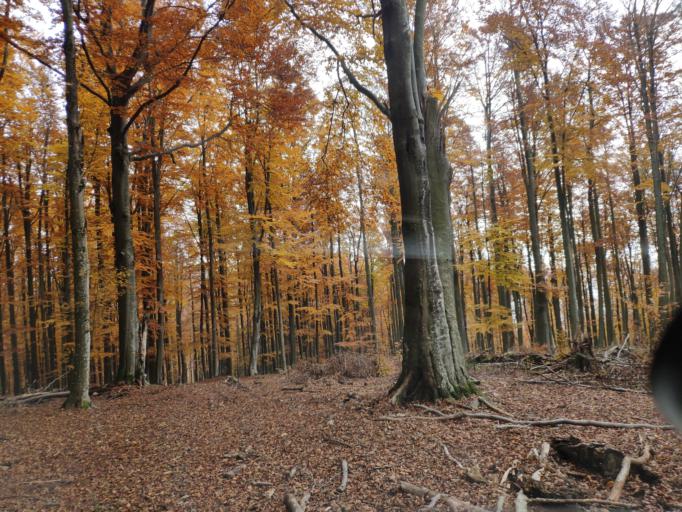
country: SK
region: Kosicky
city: Moldava nad Bodvou
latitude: 48.7345
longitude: 21.0134
